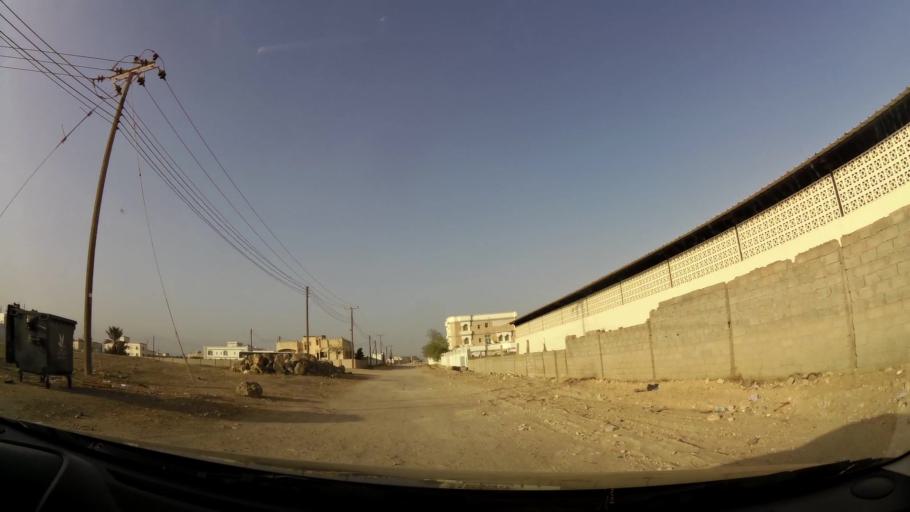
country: OM
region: Zufar
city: Salalah
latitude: 16.9959
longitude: 54.0220
